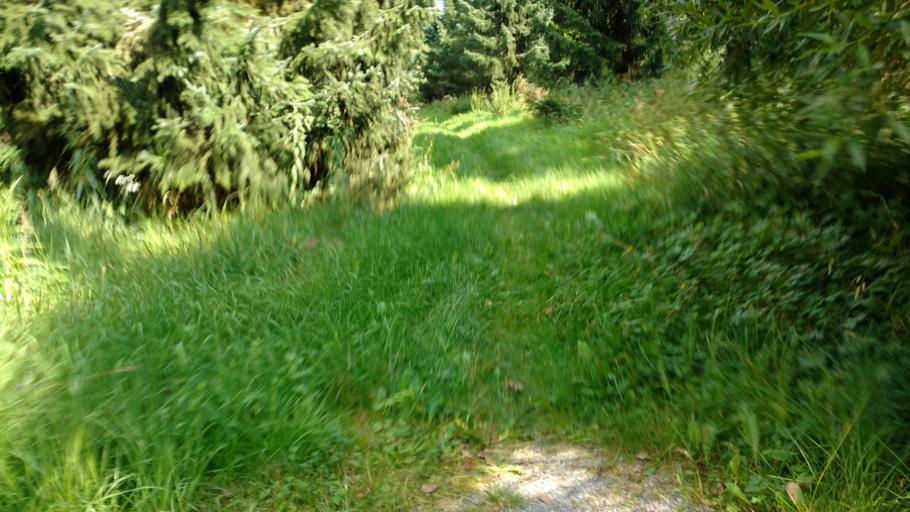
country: FI
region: Varsinais-Suomi
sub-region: Salo
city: Salo
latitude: 60.3913
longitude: 23.1465
